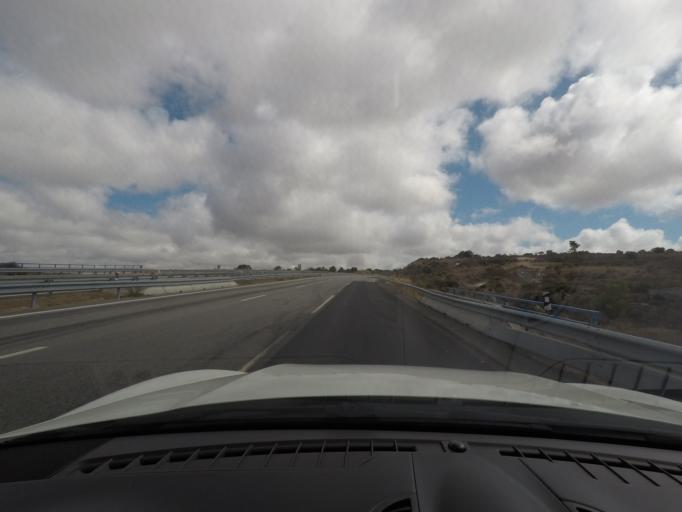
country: ES
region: Castille and Leon
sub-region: Provincia de Salamanca
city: Fuentes de Onoro
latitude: 40.6123
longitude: -6.9004
